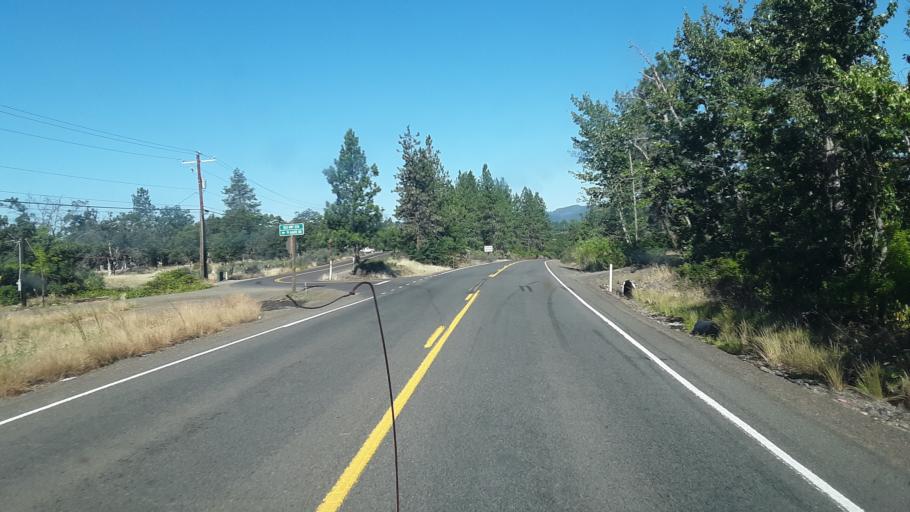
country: US
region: Oregon
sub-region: Jackson County
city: Eagle Point
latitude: 42.5237
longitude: -122.8337
